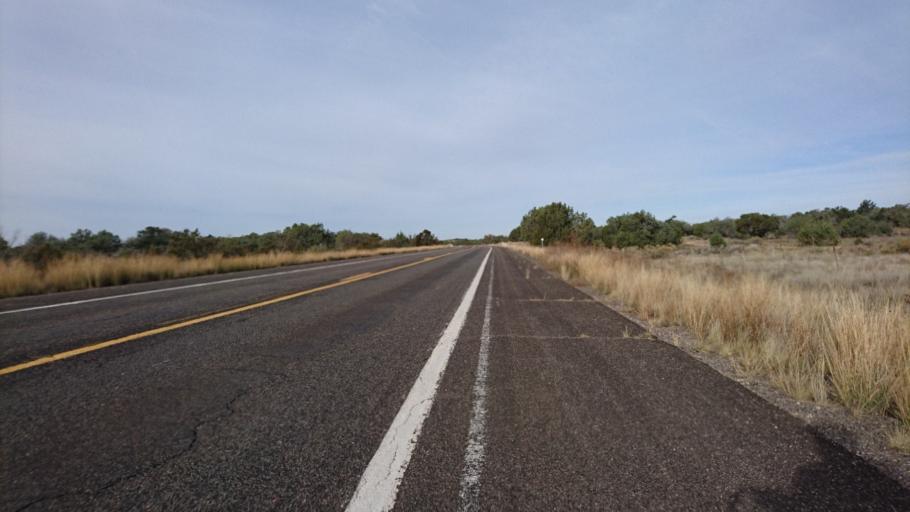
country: US
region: Arizona
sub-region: Mohave County
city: Peach Springs
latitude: 35.5536
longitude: -113.3702
